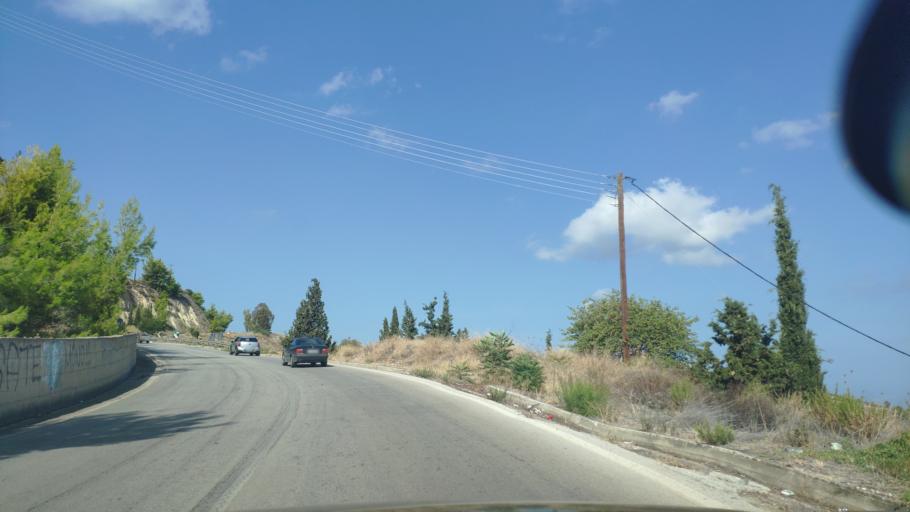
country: GR
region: Peloponnese
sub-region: Nomos Korinthias
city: Moulki
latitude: 37.9989
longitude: 22.7171
